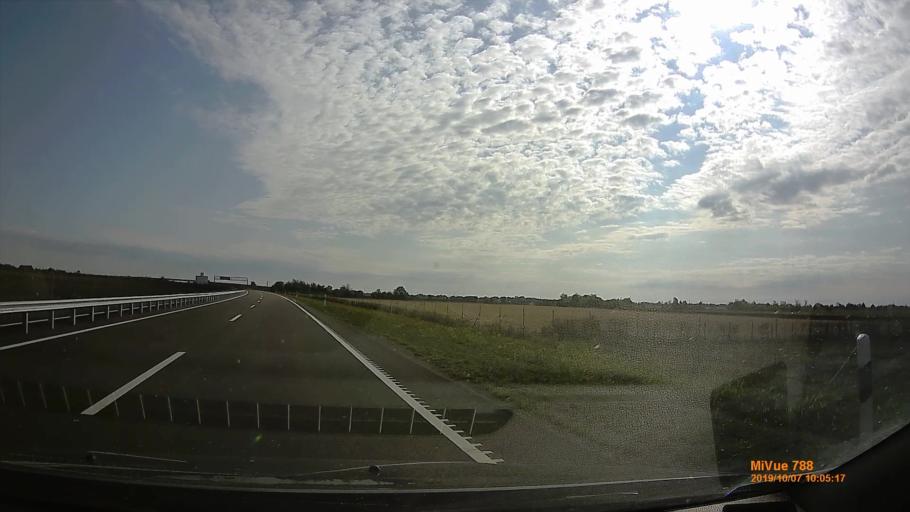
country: HU
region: Bekes
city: Kondoros
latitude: 46.7374
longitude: 20.7951
